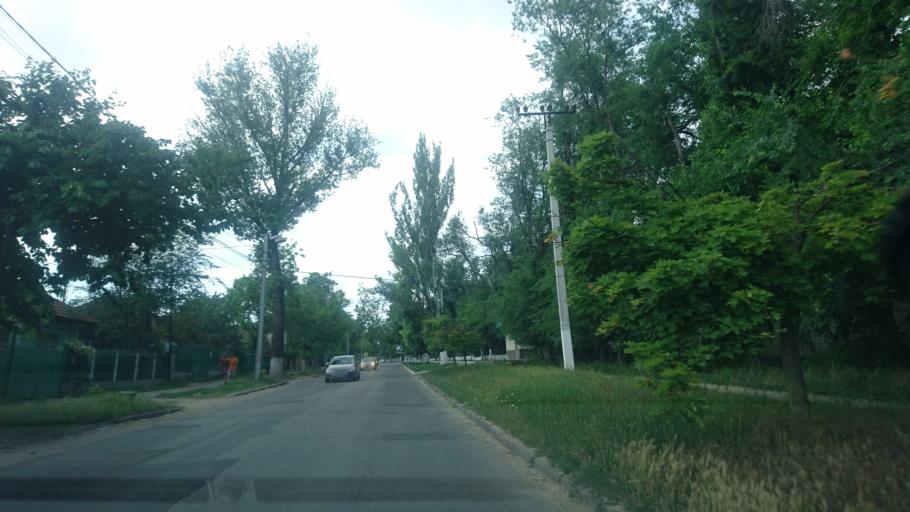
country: MD
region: Chisinau
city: Stauceni
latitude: 47.0556
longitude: 28.8407
